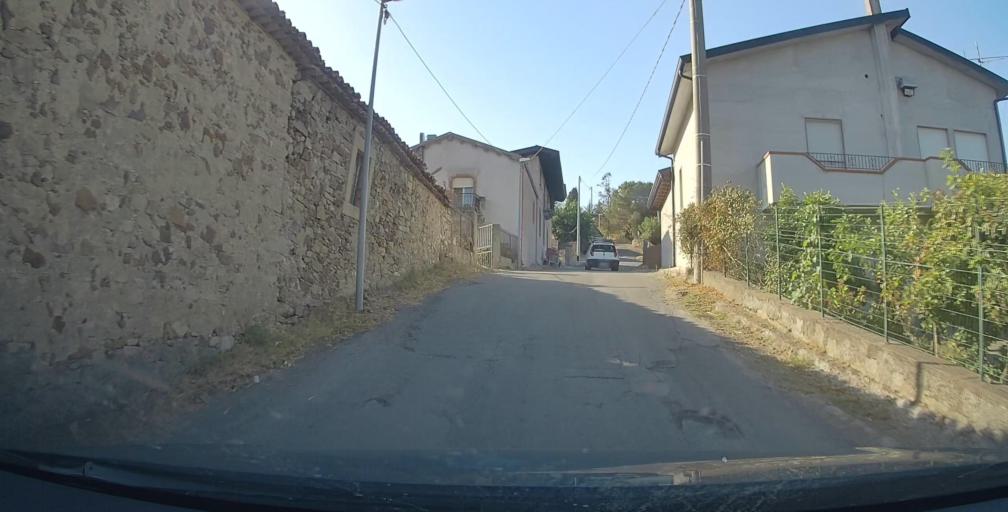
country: IT
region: Sicily
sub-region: Messina
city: San Piero Patti
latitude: 38.0593
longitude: 14.9929
